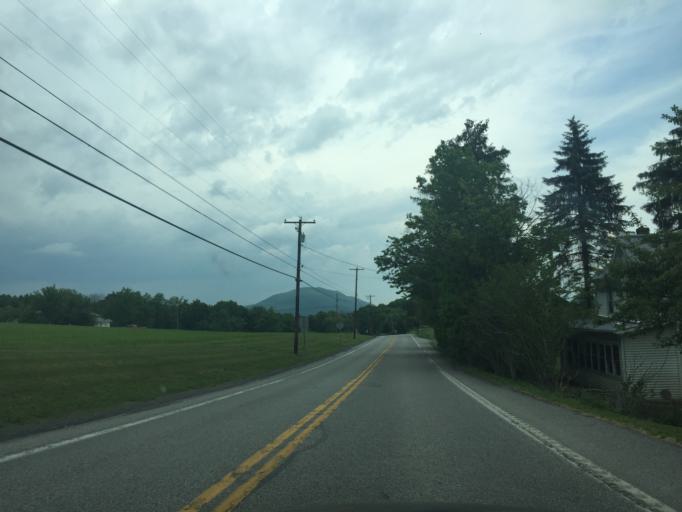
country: US
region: Pennsylvania
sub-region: Fulton County
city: McConnellsburg
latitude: 40.0355
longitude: -77.9690
